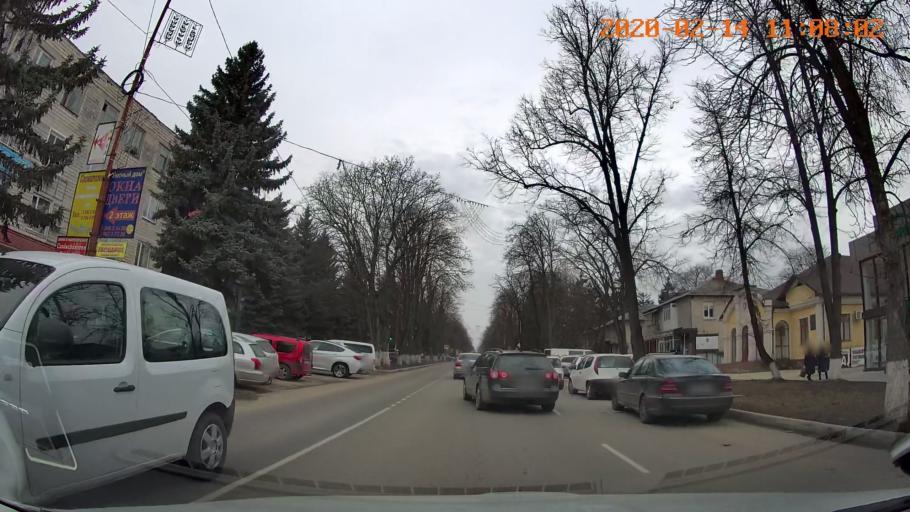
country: MD
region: Raionul Edinet
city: Edinet
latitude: 48.1705
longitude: 27.3045
